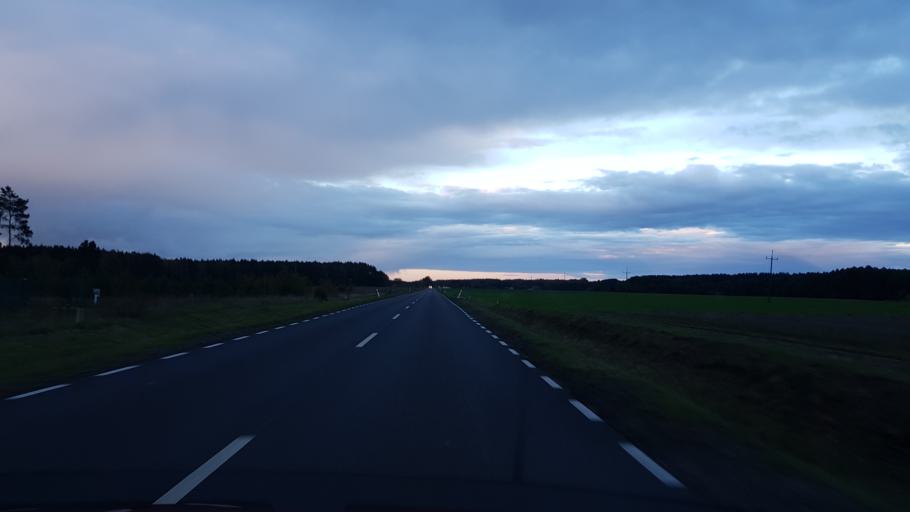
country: PL
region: Greater Poland Voivodeship
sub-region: Powiat zlotowski
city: Krajenka
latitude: 53.2686
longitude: 16.9314
